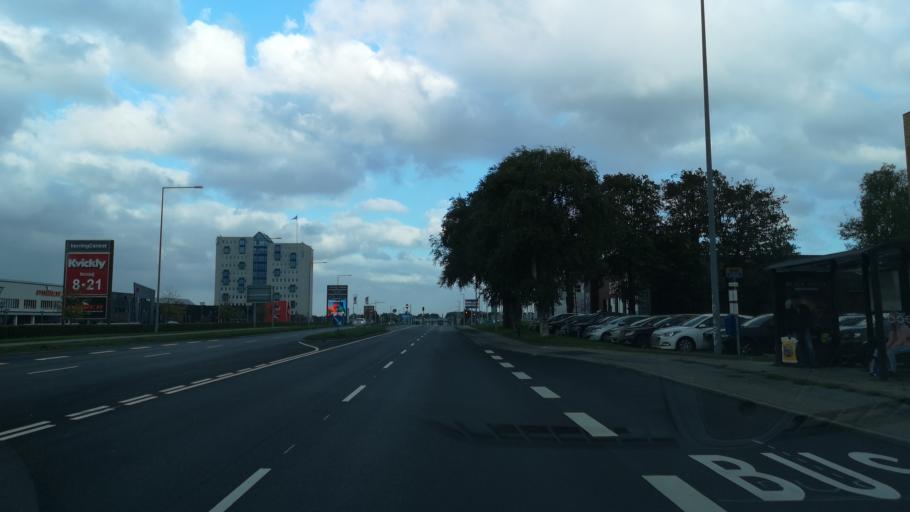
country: DK
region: Central Jutland
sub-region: Herning Kommune
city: Herning
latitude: 56.1346
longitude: 8.9963
